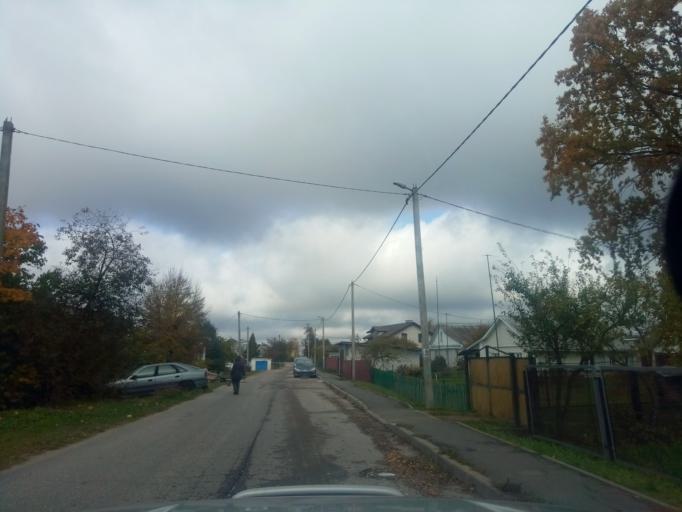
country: BY
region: Minsk
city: Zaslawye
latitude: 54.0122
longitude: 27.2943
